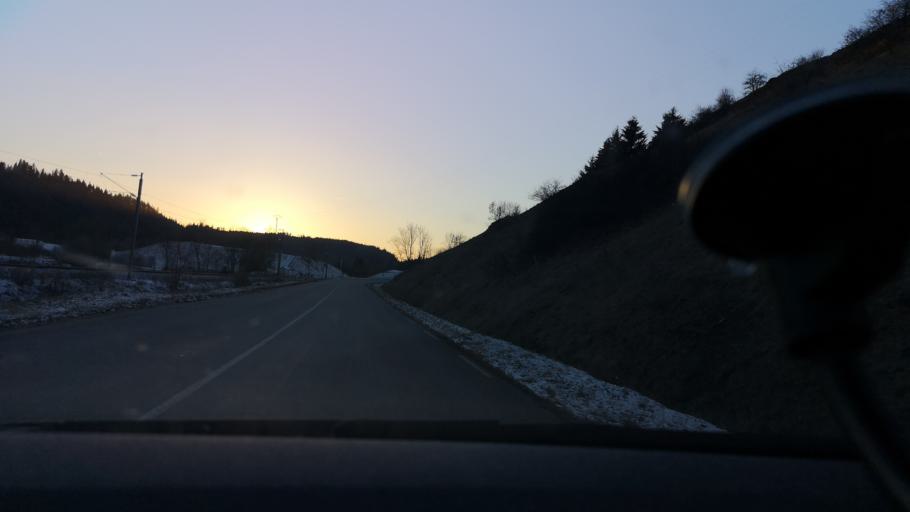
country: FR
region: Franche-Comte
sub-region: Departement du Doubs
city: La Cluse-et-Mijoux
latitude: 46.8739
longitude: 6.3967
